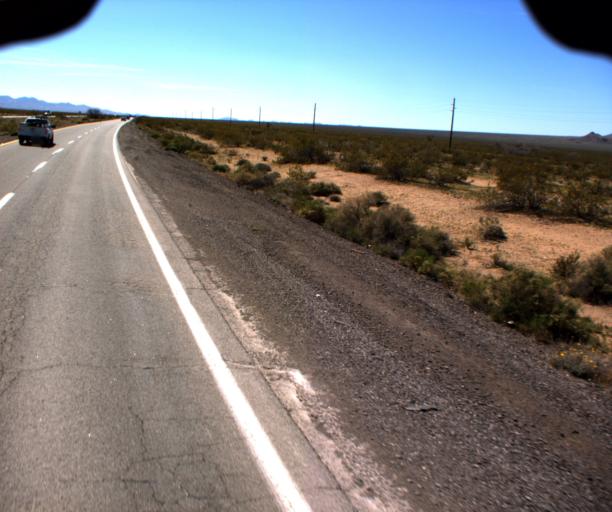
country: US
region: Arizona
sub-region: Mohave County
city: Dolan Springs
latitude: 35.6606
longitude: -114.4495
